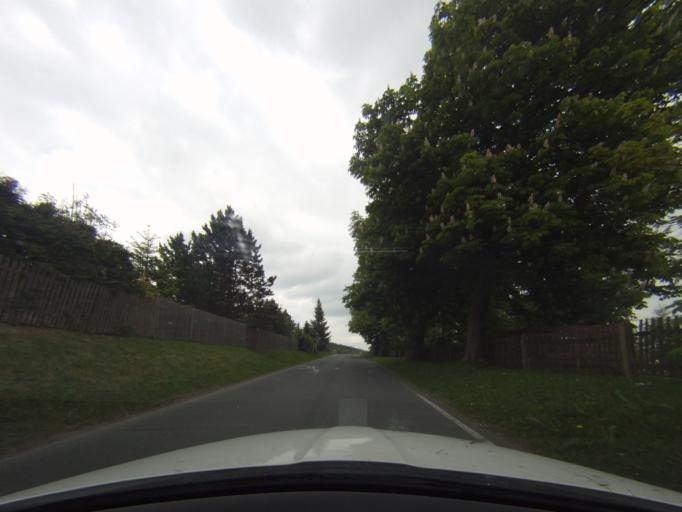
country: DE
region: Thuringia
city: Gillersdorf
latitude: 50.6074
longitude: 11.0173
